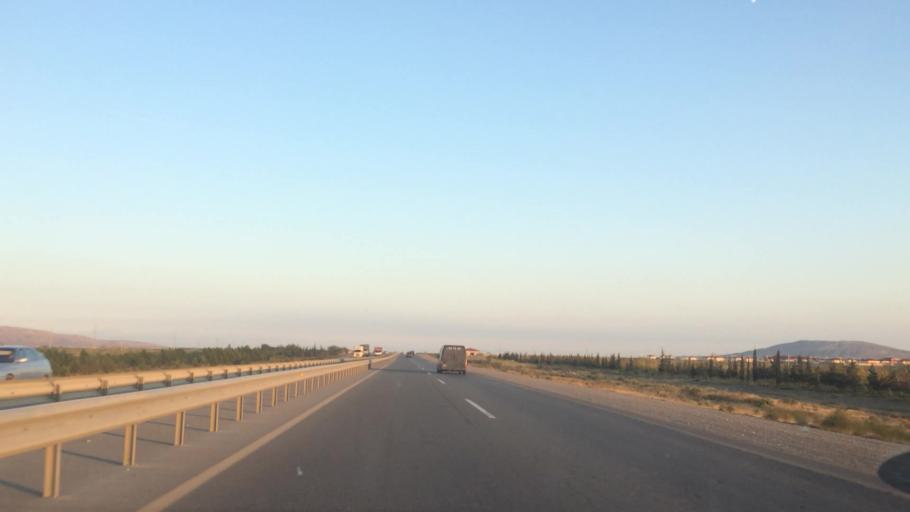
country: AZ
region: Baki
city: Qobustan
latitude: 39.9878
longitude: 49.2044
